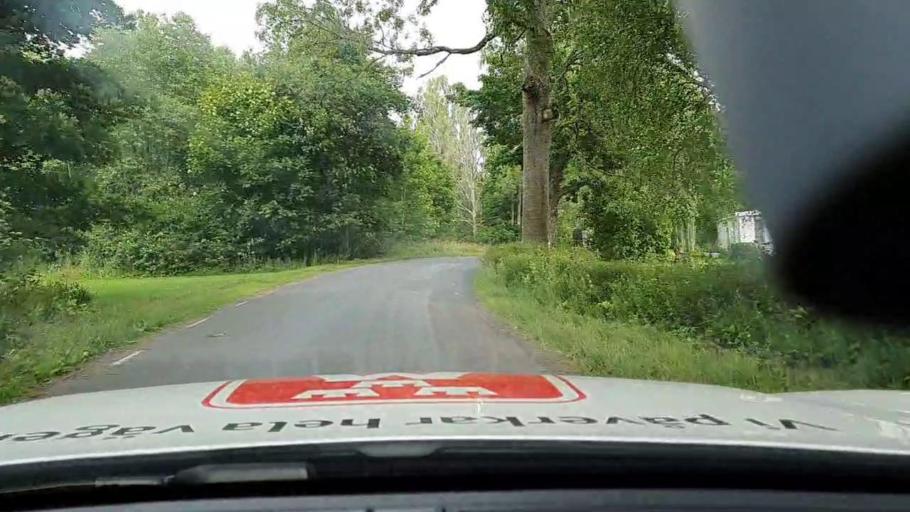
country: SE
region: Vaestra Goetaland
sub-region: Karlsborgs Kommun
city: Molltorp
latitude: 58.6107
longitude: 14.3518
